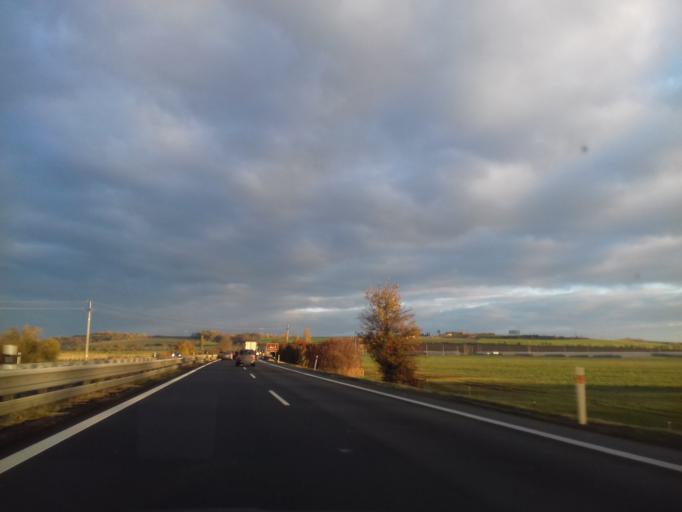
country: CZ
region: Olomoucky
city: Hnevotin
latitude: 49.5378
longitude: 17.1756
